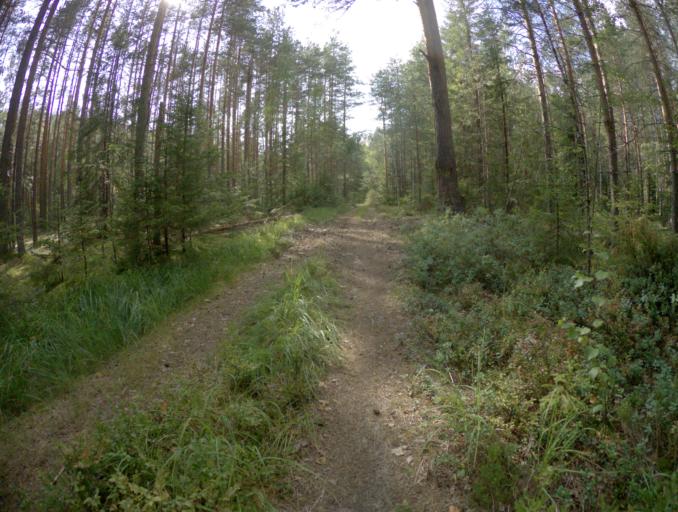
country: RU
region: Vladimir
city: Sobinka
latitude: 55.9192
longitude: 40.0809
